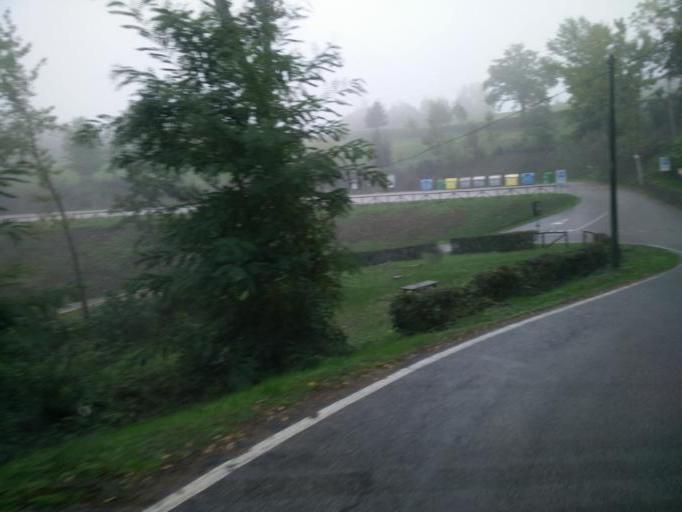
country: IT
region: Emilia-Romagna
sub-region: Provincia di Bologna
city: Marzabotto
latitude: 44.3103
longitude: 11.1968
